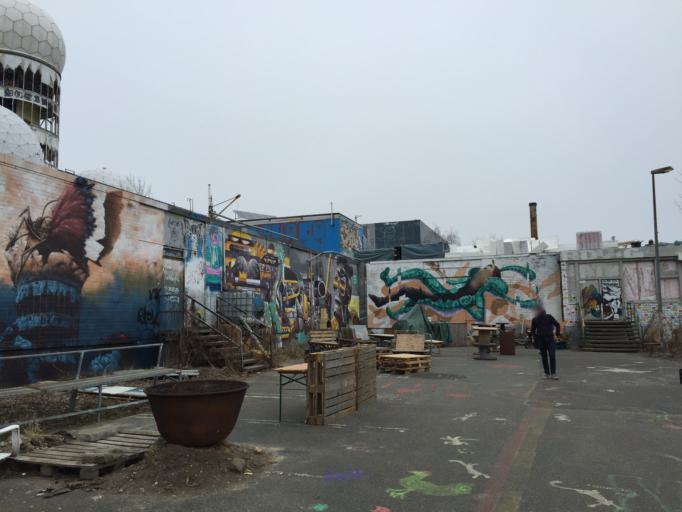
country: DE
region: Berlin
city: Grunewald
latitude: 52.4971
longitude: 13.2399
